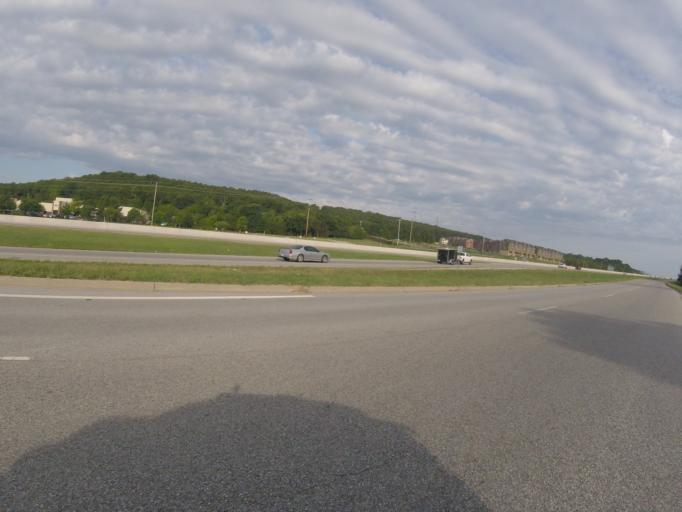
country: US
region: Arkansas
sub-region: Washington County
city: Fayetteville
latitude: 36.0595
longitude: -94.1968
